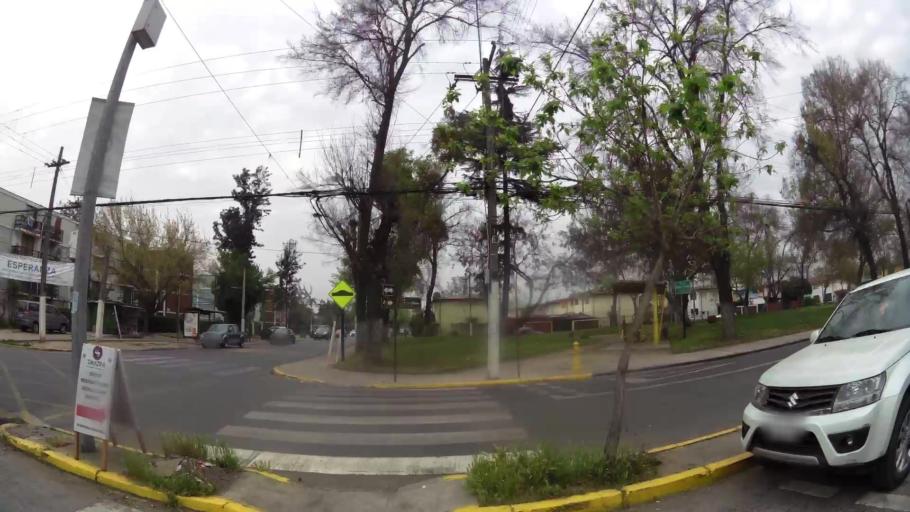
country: CL
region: Santiago Metropolitan
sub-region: Provincia de Santiago
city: Villa Presidente Frei, Nunoa, Santiago, Chile
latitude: -33.4869
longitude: -70.6061
